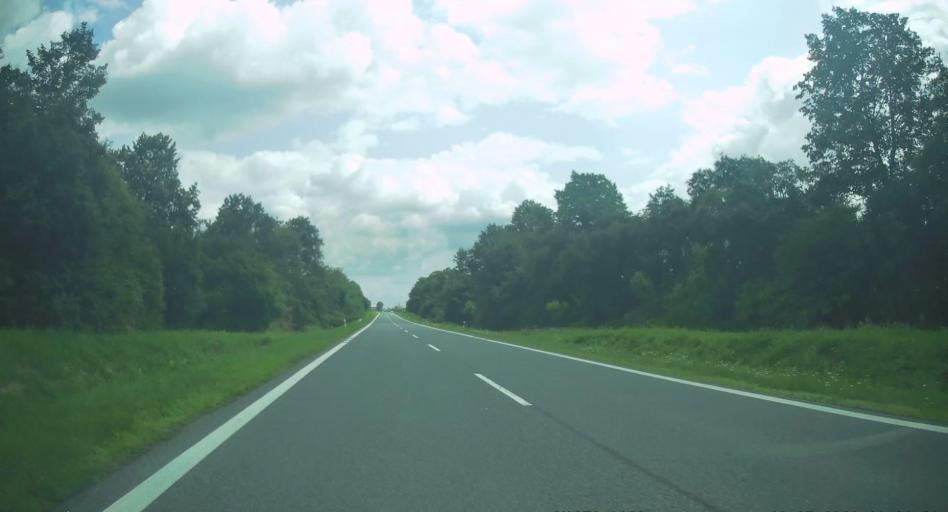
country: PL
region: Opole Voivodeship
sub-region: Powiat prudnicki
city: Lubrza
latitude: 50.3306
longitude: 17.6662
